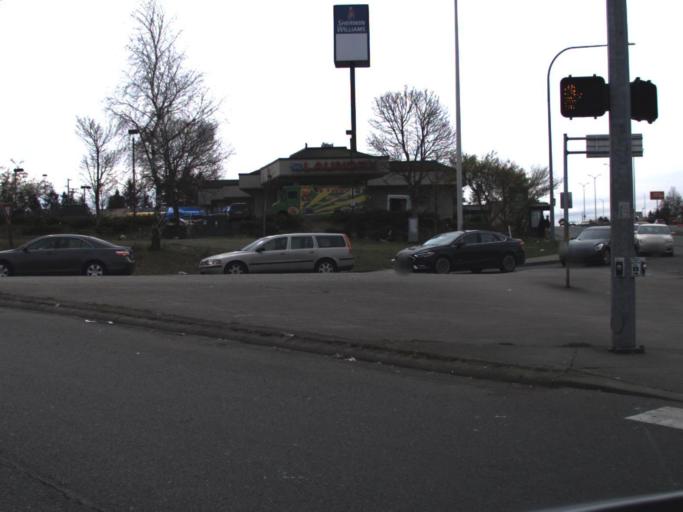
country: US
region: Washington
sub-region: King County
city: Des Moines
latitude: 47.3931
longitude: -122.2942
